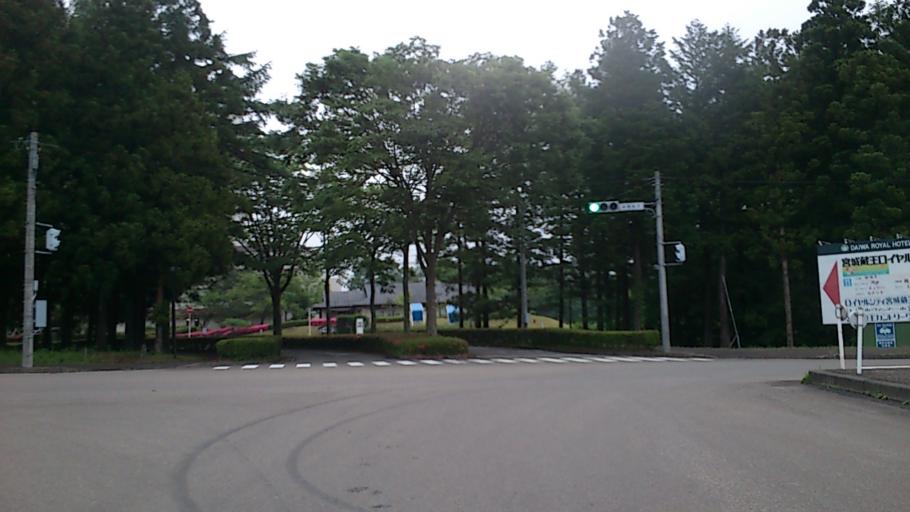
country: JP
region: Miyagi
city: Shiroishi
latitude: 38.1304
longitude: 140.5601
